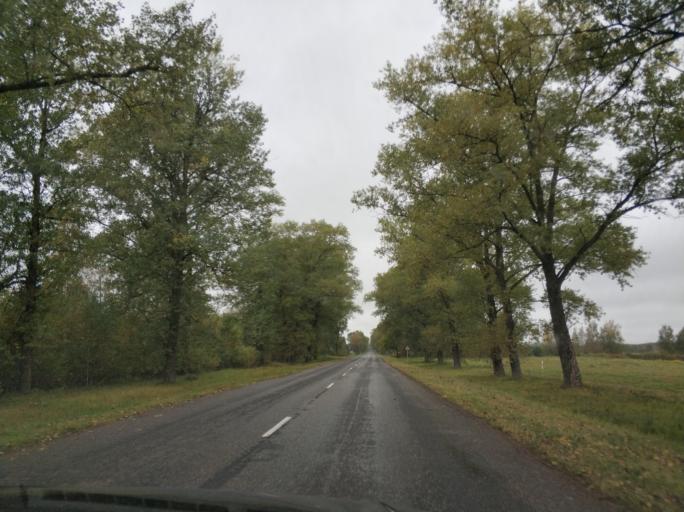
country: BY
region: Vitebsk
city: Polatsk
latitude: 55.4366
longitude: 28.9722
